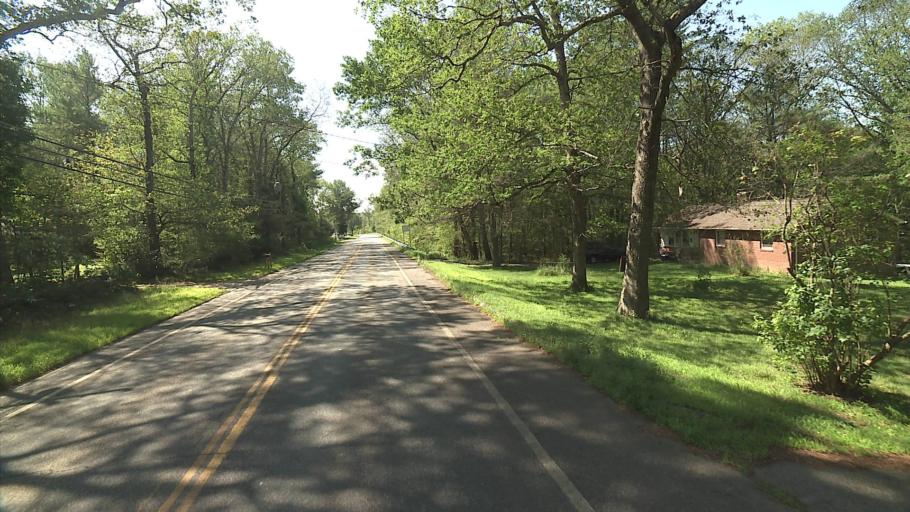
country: US
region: Connecticut
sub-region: Tolland County
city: Storrs
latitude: 41.8951
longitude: -72.1701
